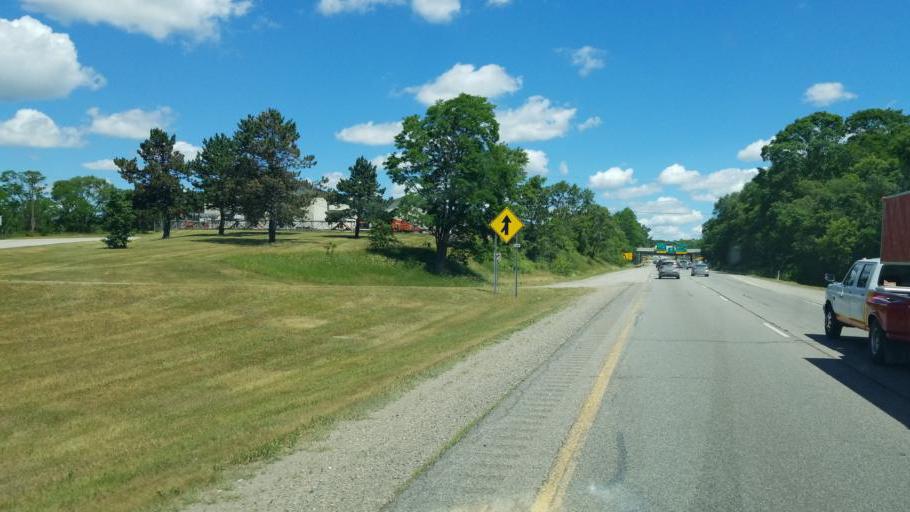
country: US
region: Michigan
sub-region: Livingston County
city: Brighton
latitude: 42.5174
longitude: -83.7566
